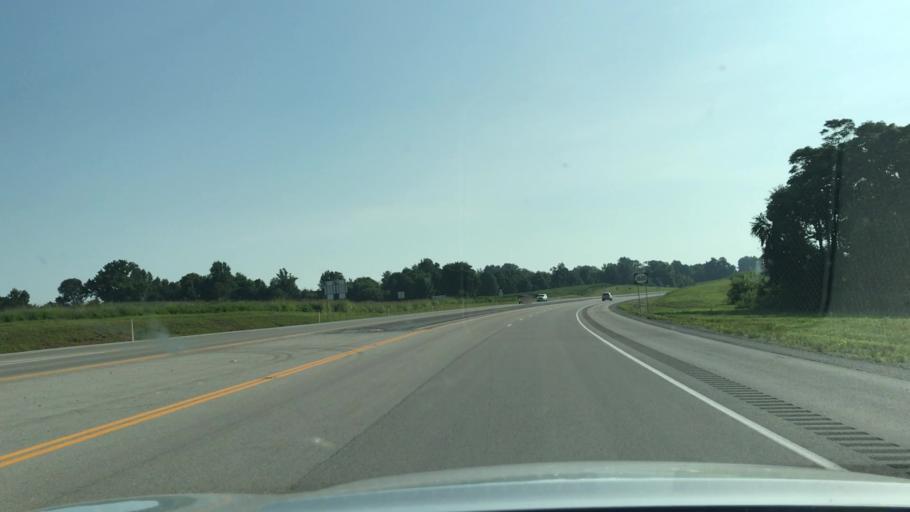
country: US
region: Kentucky
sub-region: Barren County
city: Glasgow
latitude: 36.9948
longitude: -85.9785
